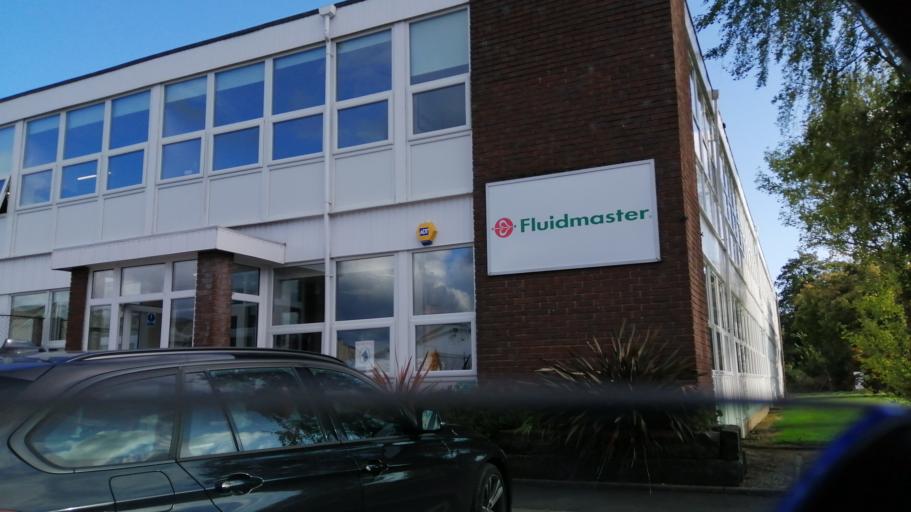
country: GB
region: England
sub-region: Herefordshire
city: Lower Bullingham
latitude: 52.0367
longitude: -2.6954
